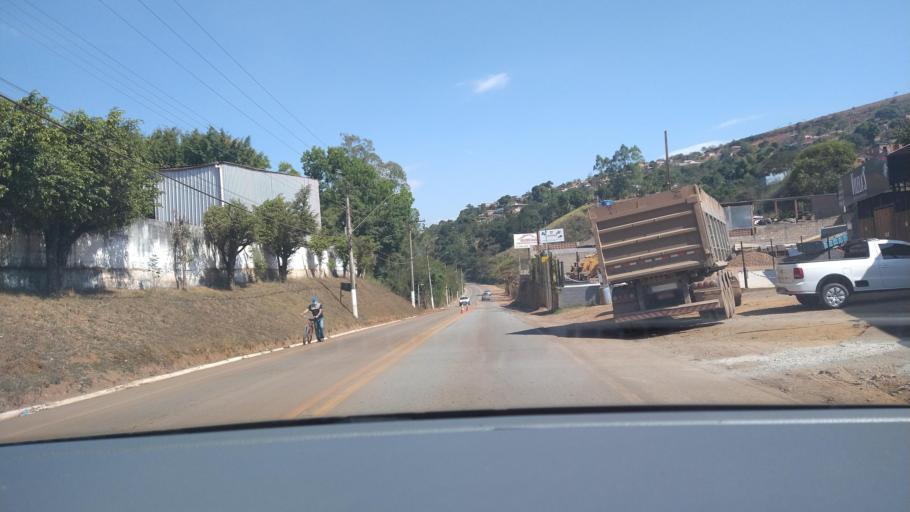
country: BR
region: Minas Gerais
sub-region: Rio Piracicaba
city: Rio Piracicaba
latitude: -19.9197
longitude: -43.1613
